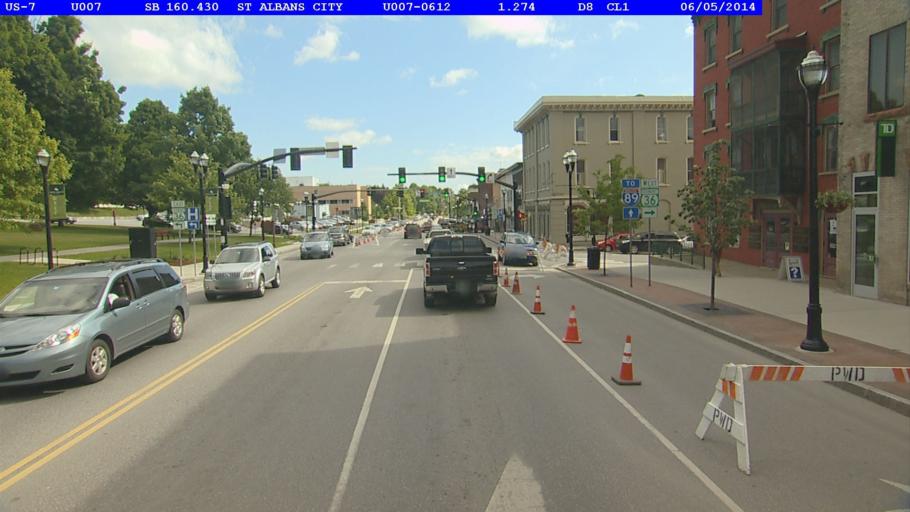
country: US
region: Vermont
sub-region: Franklin County
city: Saint Albans
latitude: 44.8111
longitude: -73.0834
